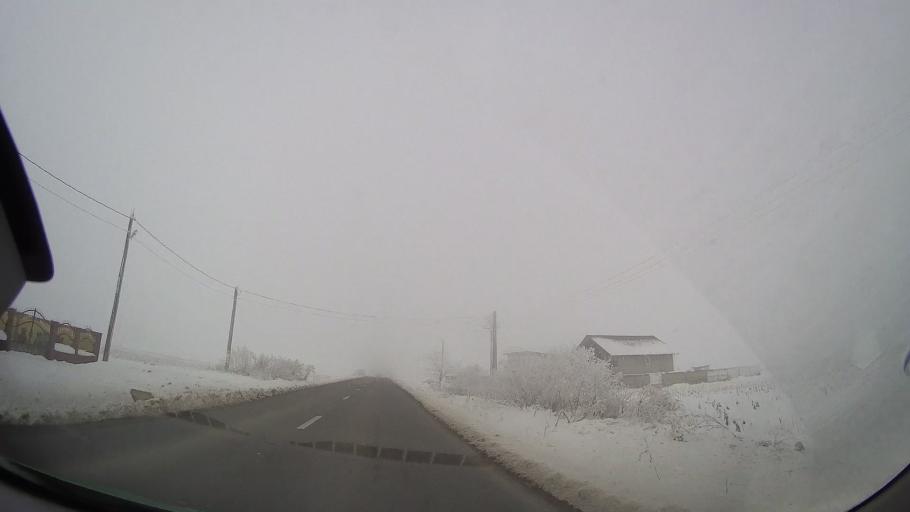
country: RO
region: Iasi
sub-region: Comuna Mogosesti-Siret
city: Mogosesti-Siret
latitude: 47.1421
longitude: 26.7795
